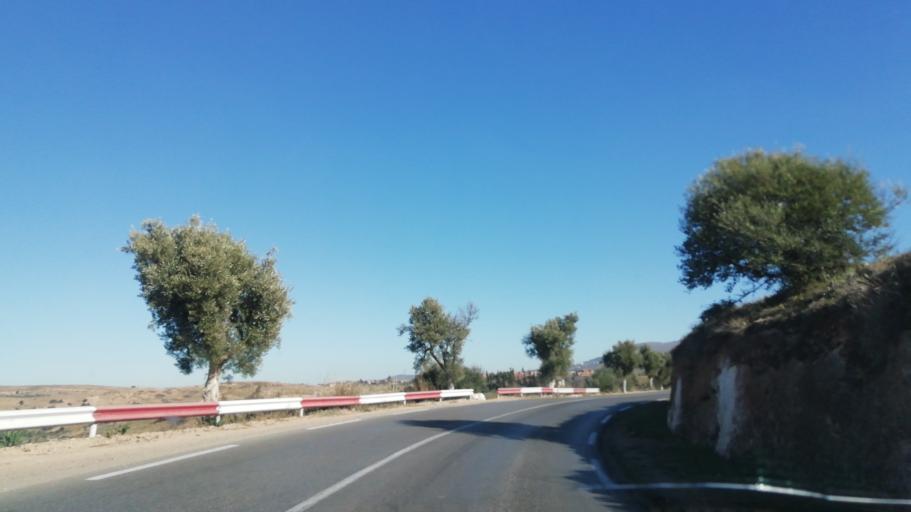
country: DZ
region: Tlemcen
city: Beni Mester
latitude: 34.8396
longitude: -1.4874
